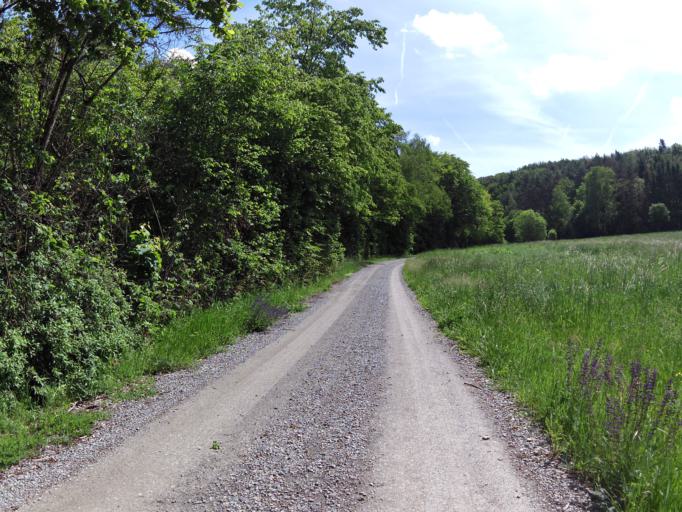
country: DE
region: Bavaria
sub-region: Regierungsbezirk Unterfranken
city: Winterhausen
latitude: 49.7209
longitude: 10.0255
